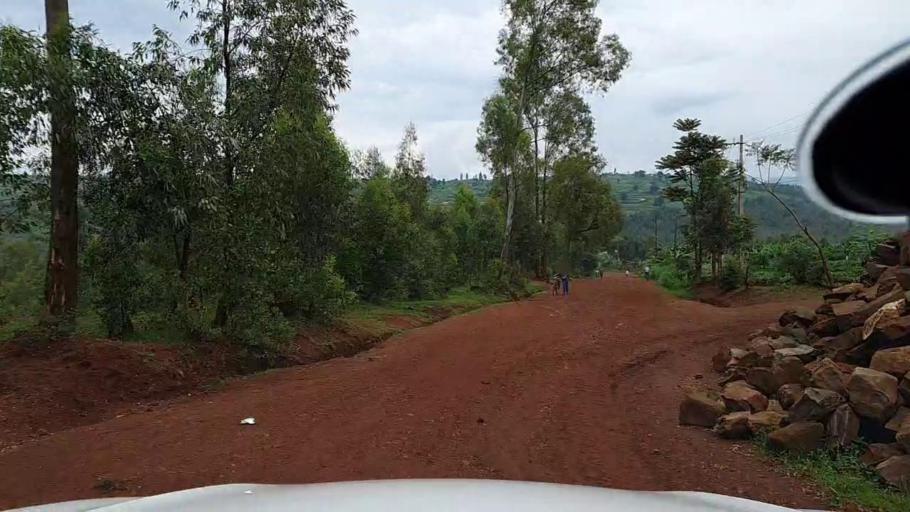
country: RW
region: Kigali
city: Kigali
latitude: -1.9086
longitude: 29.8982
